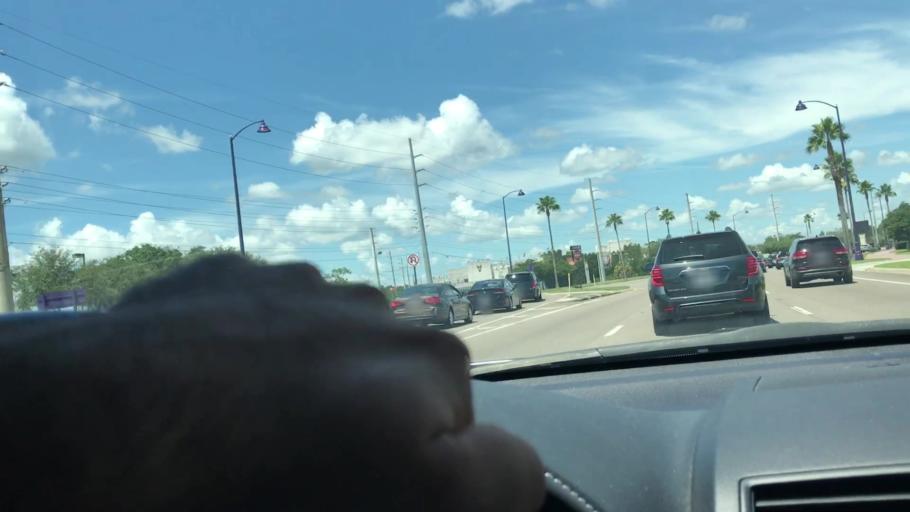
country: US
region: Florida
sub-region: Osceola County
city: Kissimmee
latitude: 28.3041
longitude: -81.4598
